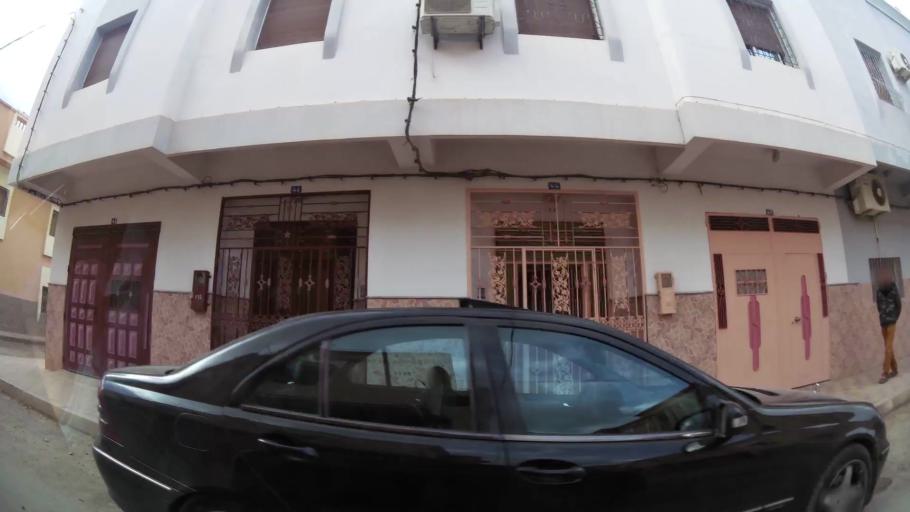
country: MA
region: Oriental
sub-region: Nador
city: Nador
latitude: 35.1603
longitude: -2.9174
